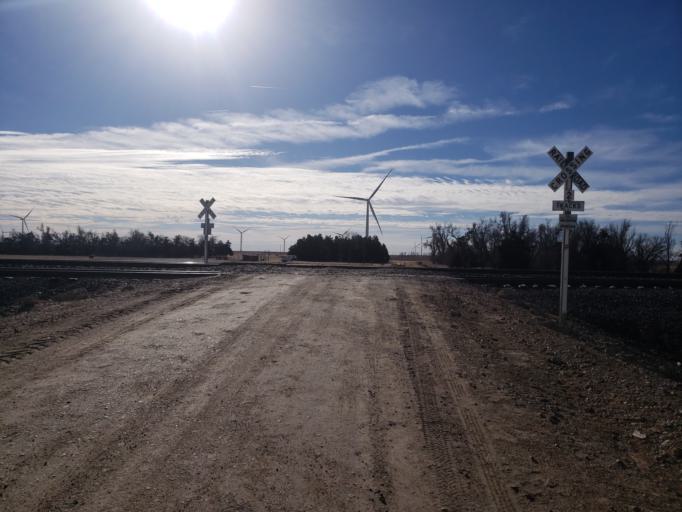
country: US
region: Kansas
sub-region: Edwards County
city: Kinsley
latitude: 37.8726
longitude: -99.6577
